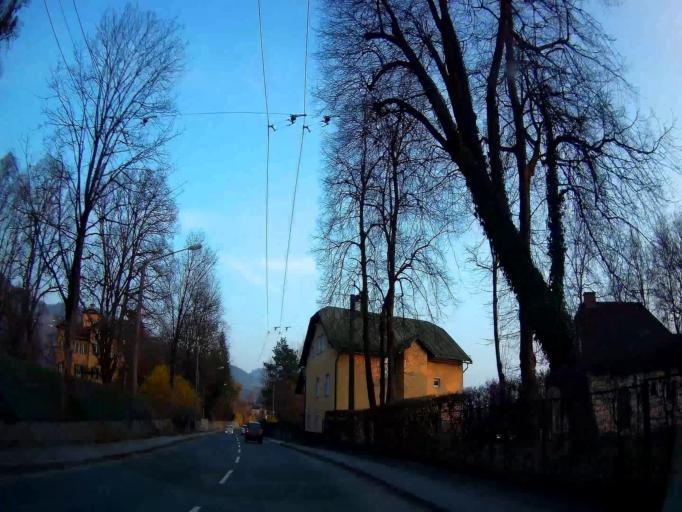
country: AT
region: Salzburg
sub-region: Salzburg Stadt
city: Salzburg
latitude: 47.7954
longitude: 13.0701
